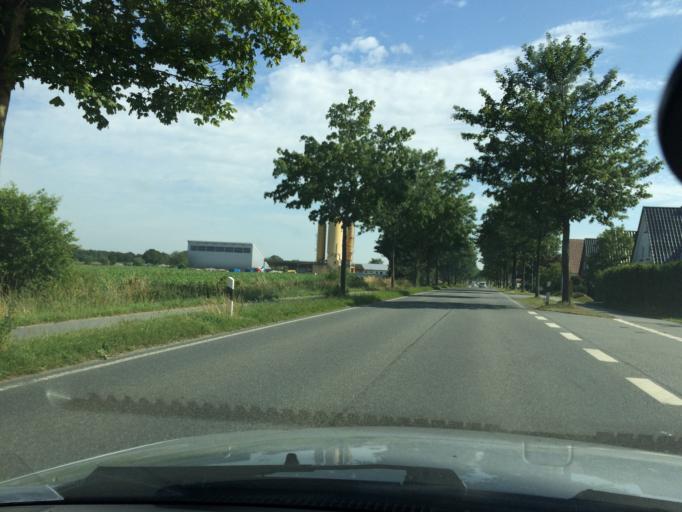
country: DE
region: Schleswig-Holstein
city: Jarplund-Weding
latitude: 54.7433
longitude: 9.4391
